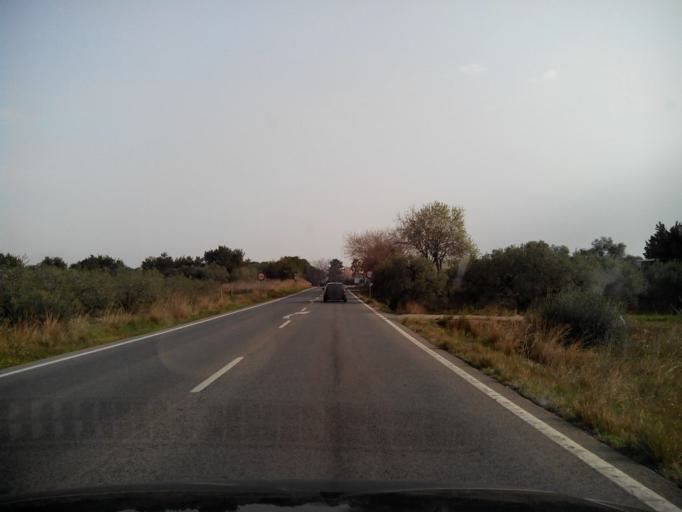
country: ES
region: Catalonia
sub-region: Provincia de Tarragona
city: Riudoms
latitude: 41.1116
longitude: 1.0911
